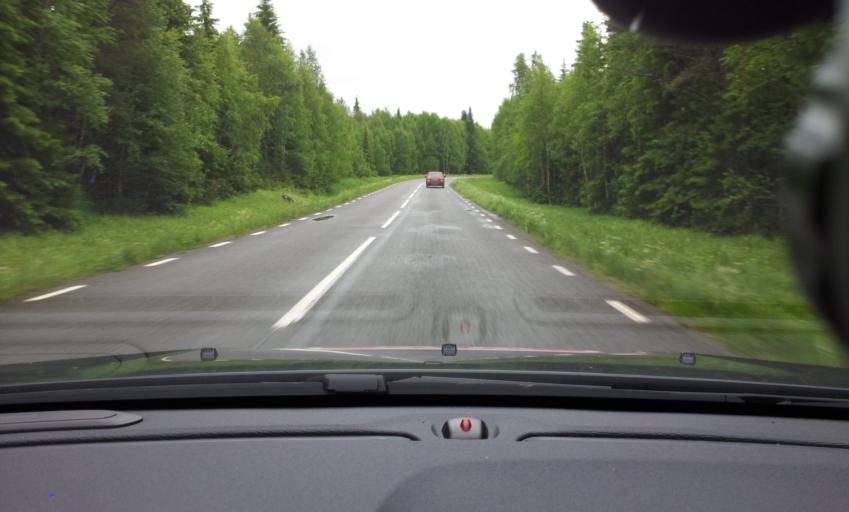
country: SE
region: Jaemtland
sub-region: Stroemsunds Kommun
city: Stroemsund
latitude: 63.4691
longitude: 15.4524
